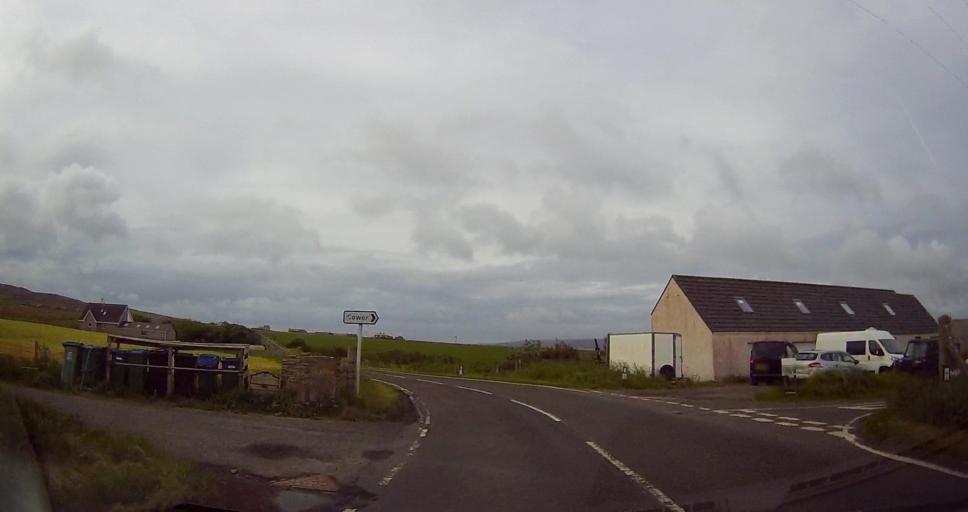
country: GB
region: Scotland
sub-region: Orkney Islands
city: Stromness
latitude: 58.9387
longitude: -3.2136
